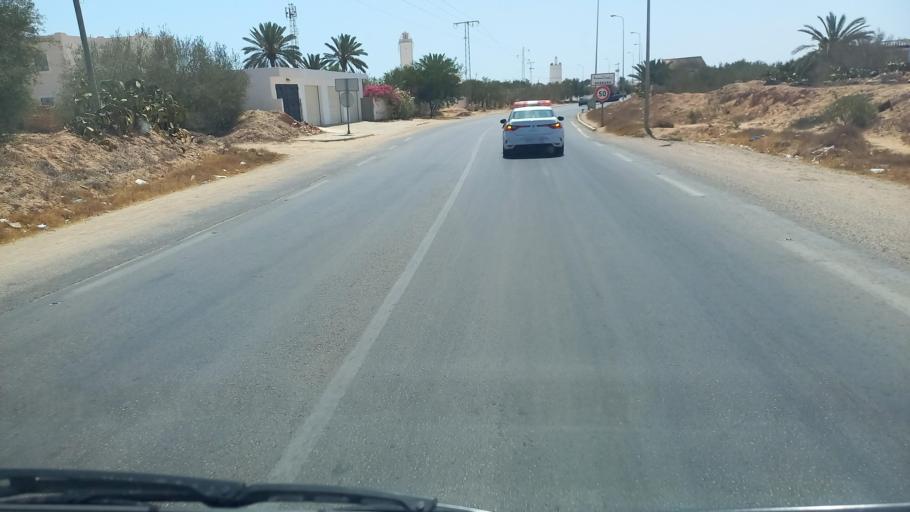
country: TN
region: Madanin
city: Houmt Souk
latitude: 33.7830
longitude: 10.8882
